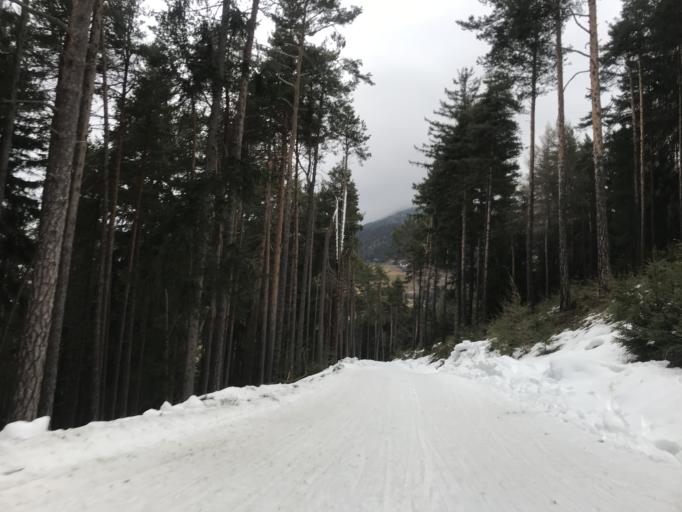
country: IT
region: Trentino-Alto Adige
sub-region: Bolzano
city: Bressanone
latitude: 46.6892
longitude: 11.6858
